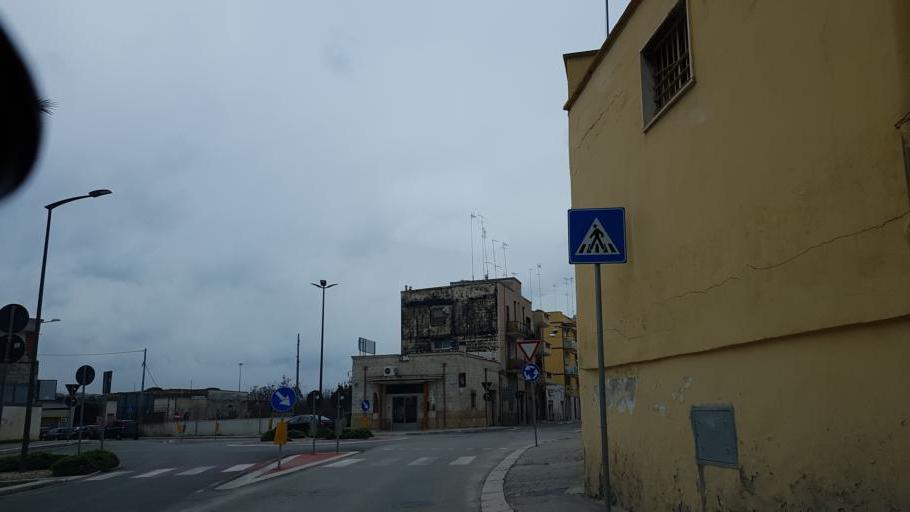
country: IT
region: Apulia
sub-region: Provincia di Brindisi
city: Brindisi
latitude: 40.6323
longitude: 17.9466
